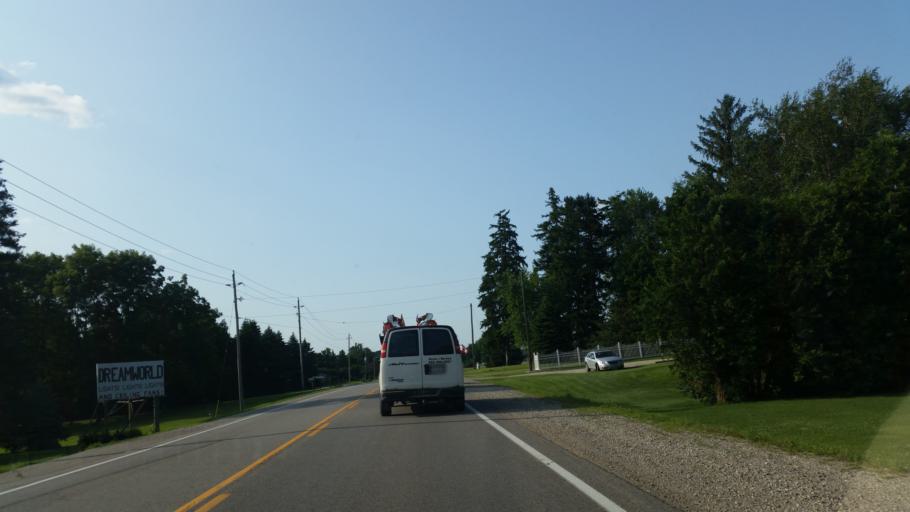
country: CA
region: Ontario
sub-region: Oxford County
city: Woodstock
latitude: 43.0045
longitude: -80.6036
